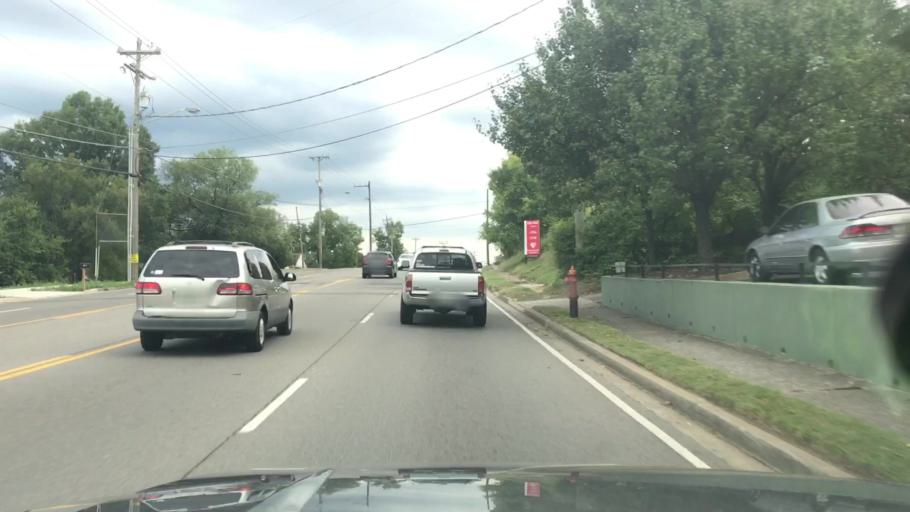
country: US
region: Tennessee
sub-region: Davidson County
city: Belle Meade
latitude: 36.1425
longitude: -86.8577
